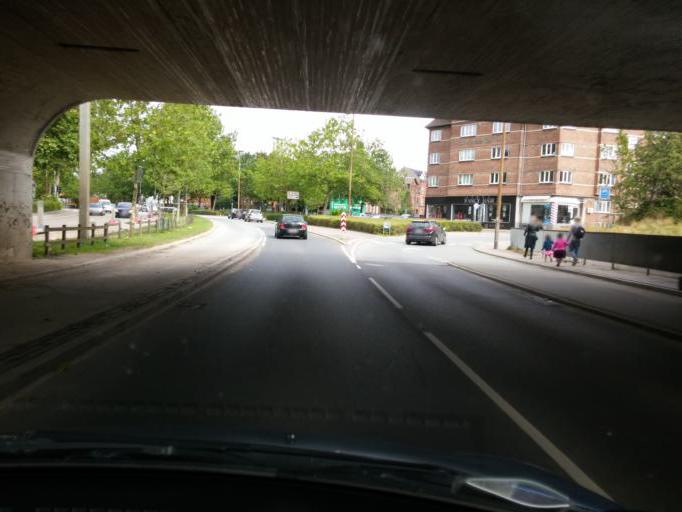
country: DK
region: South Denmark
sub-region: Odense Kommune
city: Odense
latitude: 55.4019
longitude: 10.3910
